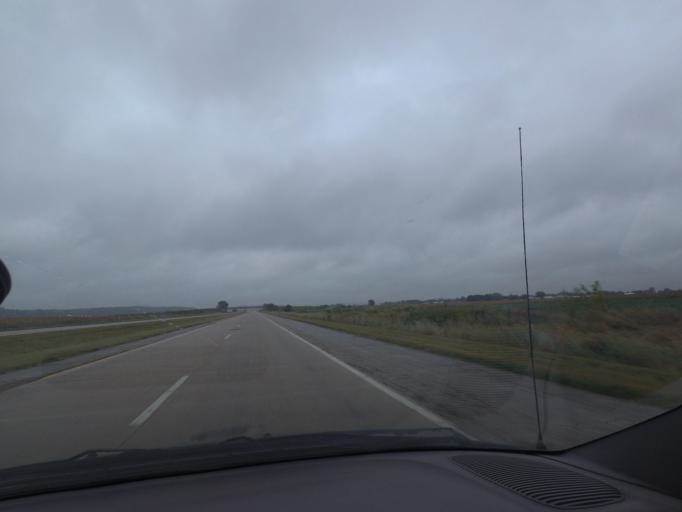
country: US
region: Illinois
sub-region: Adams County
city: Payson
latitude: 39.7216
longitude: -91.2191
